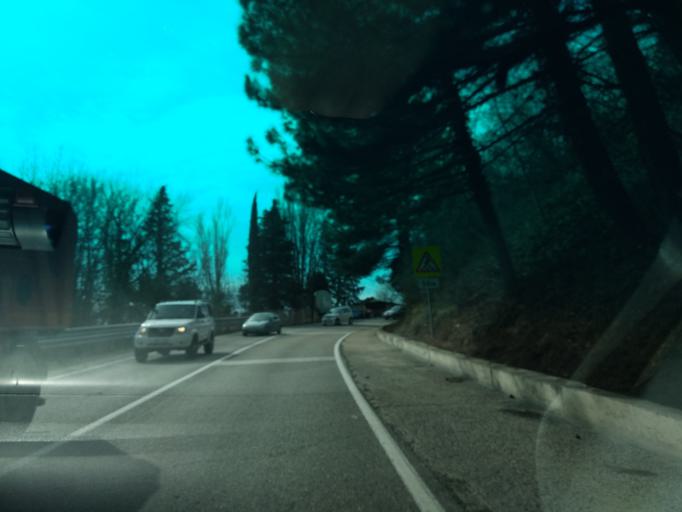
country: RU
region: Krasnodarskiy
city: Shepsi
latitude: 44.0449
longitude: 39.1363
